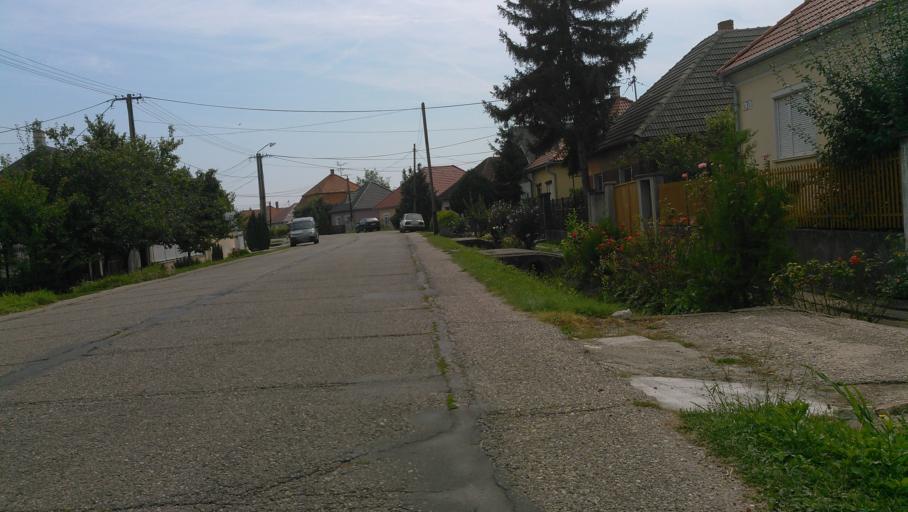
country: SK
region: Nitriansky
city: Kolarovo
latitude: 47.9077
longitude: 18.0000
